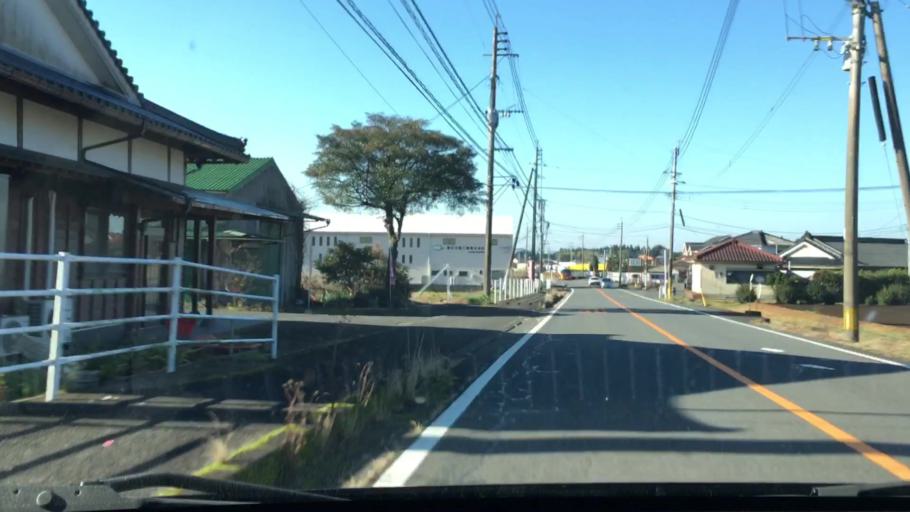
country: JP
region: Kagoshima
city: Kajiki
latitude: 31.7875
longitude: 130.7089
